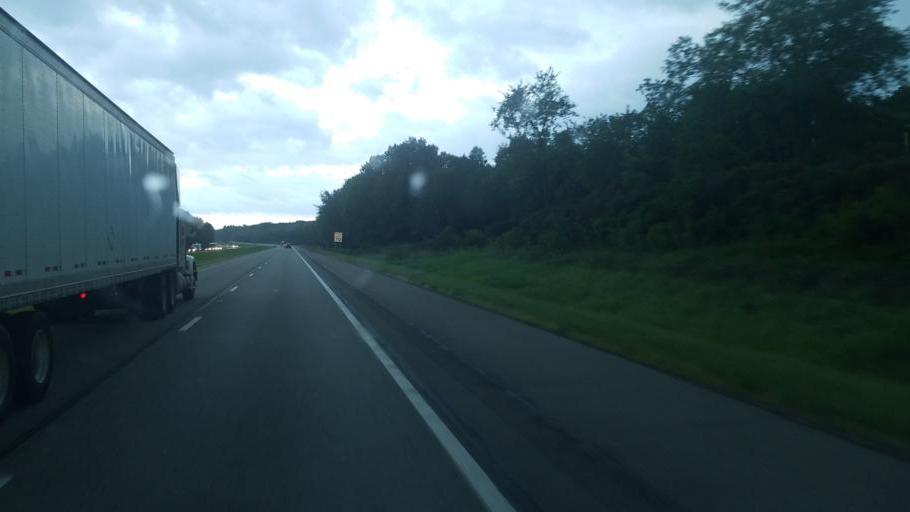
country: US
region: Pennsylvania
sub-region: Mercer County
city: Grove City
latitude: 41.0935
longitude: -80.1400
